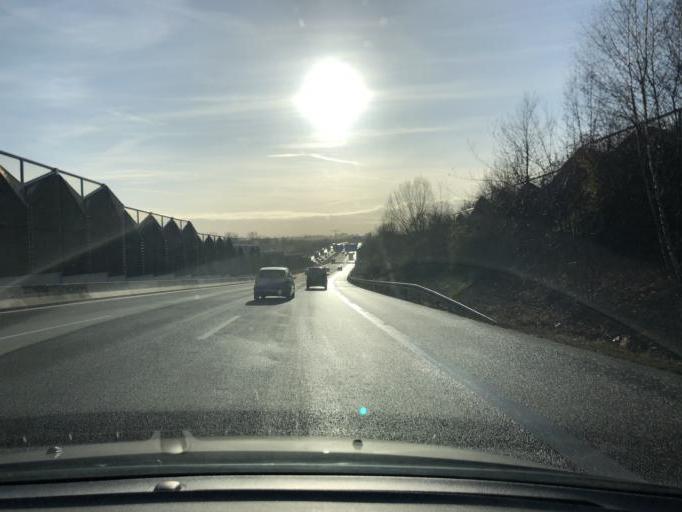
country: DE
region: Saxony
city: Neukirchen
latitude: 50.8221
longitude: 12.8543
